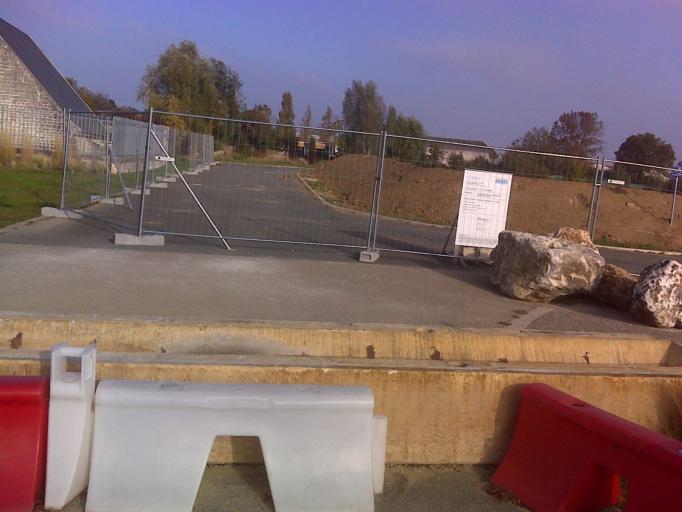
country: FR
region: Poitou-Charentes
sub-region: Departement de la Charente-Maritime
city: Echillais
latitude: 45.9274
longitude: -0.9532
